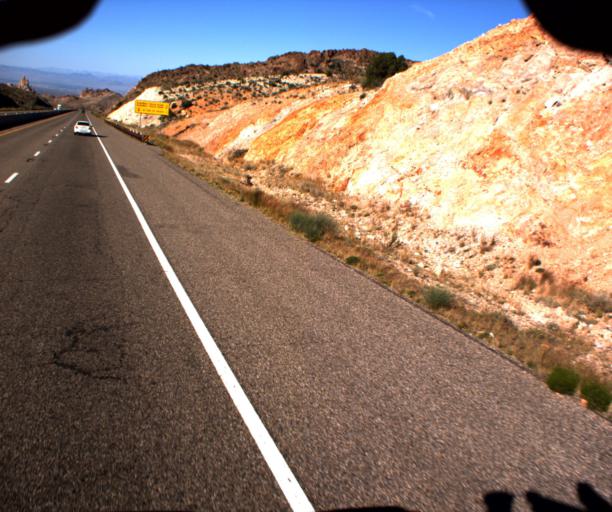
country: US
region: Arizona
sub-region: Mohave County
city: Golden Valley
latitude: 35.2153
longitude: -114.3962
